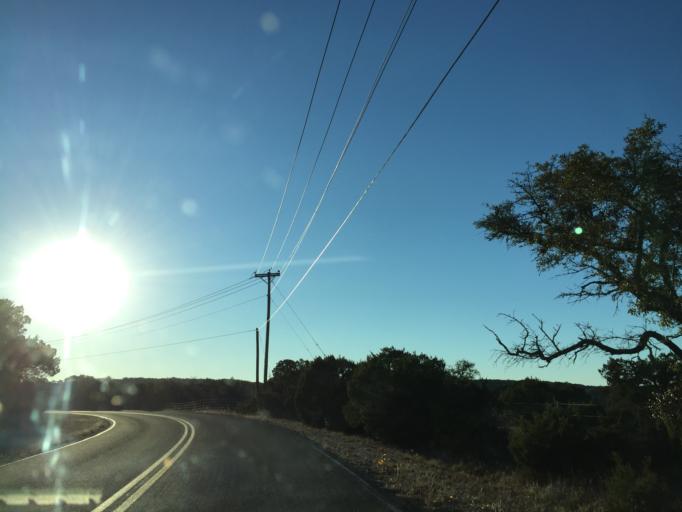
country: US
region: Texas
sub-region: Travis County
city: Lago Vista
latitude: 30.5041
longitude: -98.0529
